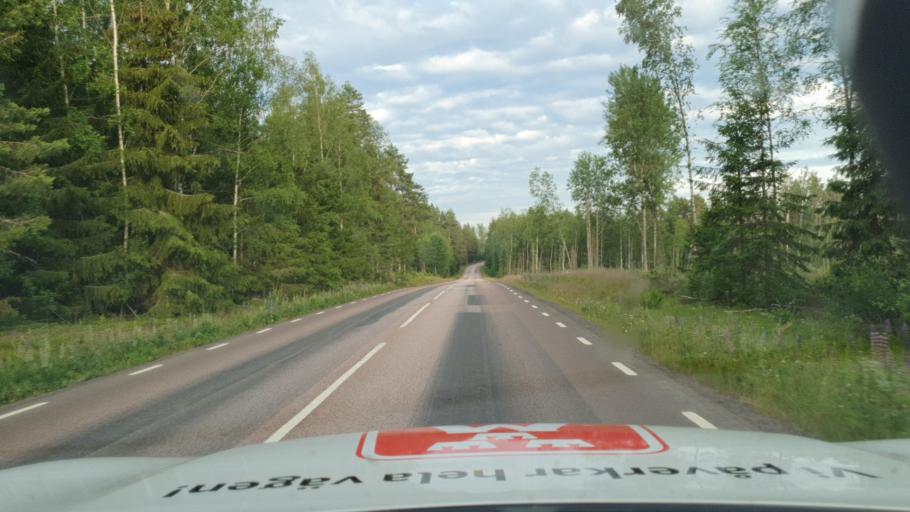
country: SE
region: Vaermland
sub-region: Karlstads Kommun
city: Molkom
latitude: 59.5360
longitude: 13.7830
